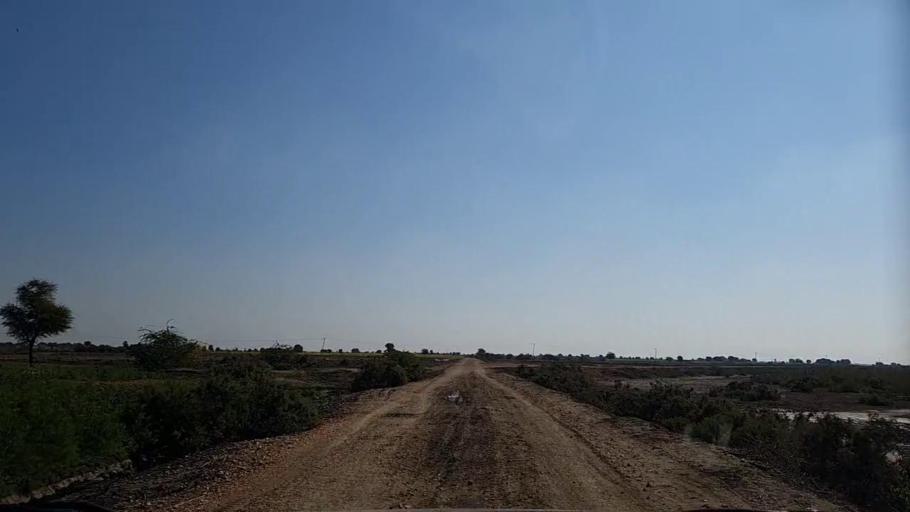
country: PK
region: Sindh
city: Pithoro
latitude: 25.6978
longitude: 69.3424
